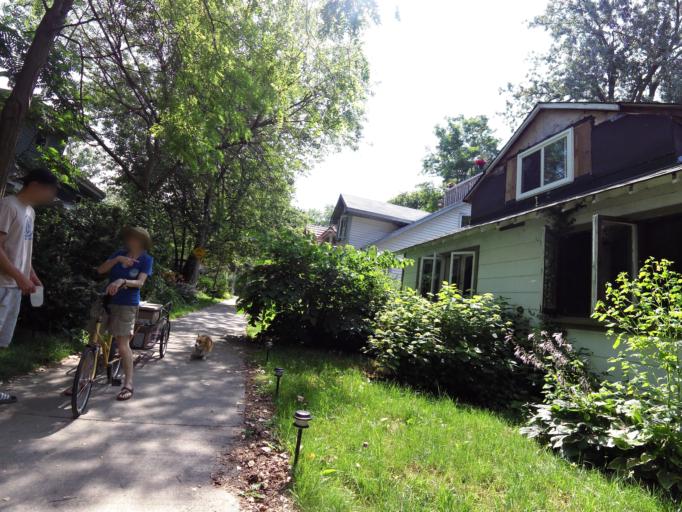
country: CA
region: Ontario
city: Toronto
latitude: 43.6330
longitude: -79.3562
